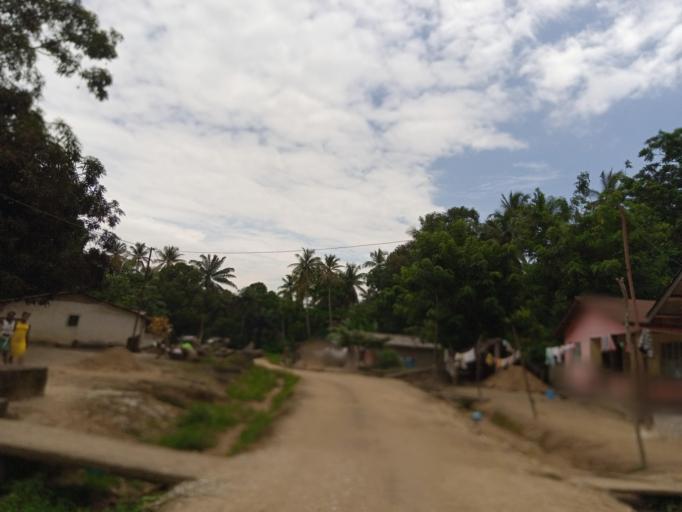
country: SL
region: Northern Province
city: Masoyila
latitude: 8.5600
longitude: -13.1689
